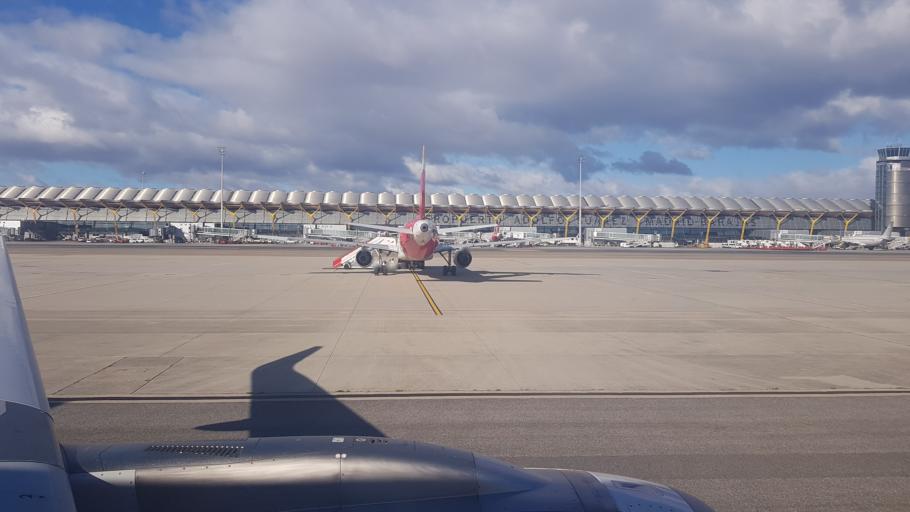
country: ES
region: Madrid
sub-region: Provincia de Madrid
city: Barajas de Madrid
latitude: 40.4900
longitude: -3.5865
